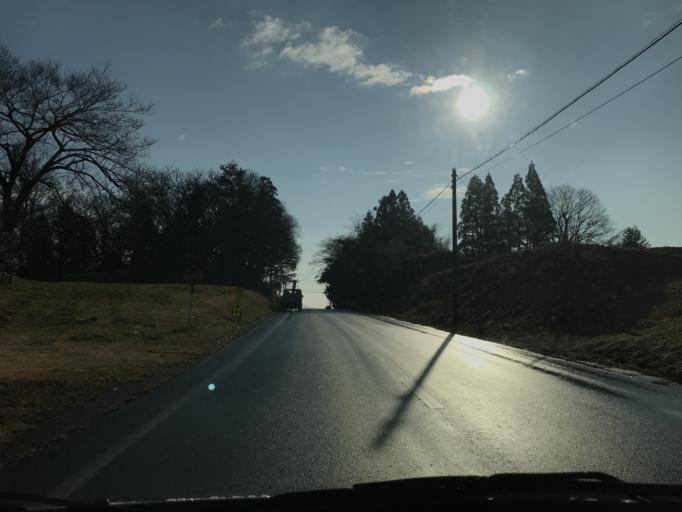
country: JP
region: Iwate
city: Ichinoseki
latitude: 38.7837
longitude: 141.1730
